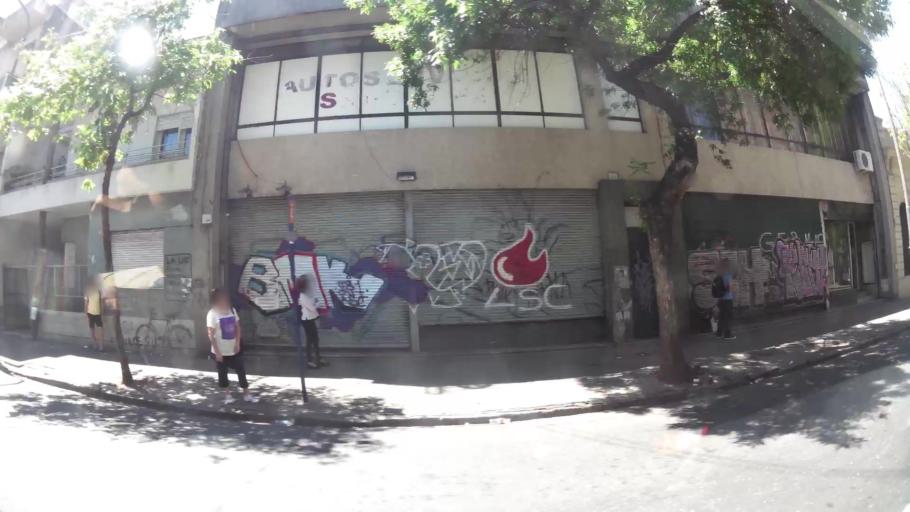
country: AR
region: Santa Fe
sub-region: Departamento de Rosario
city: Rosario
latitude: -32.9417
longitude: -60.6567
